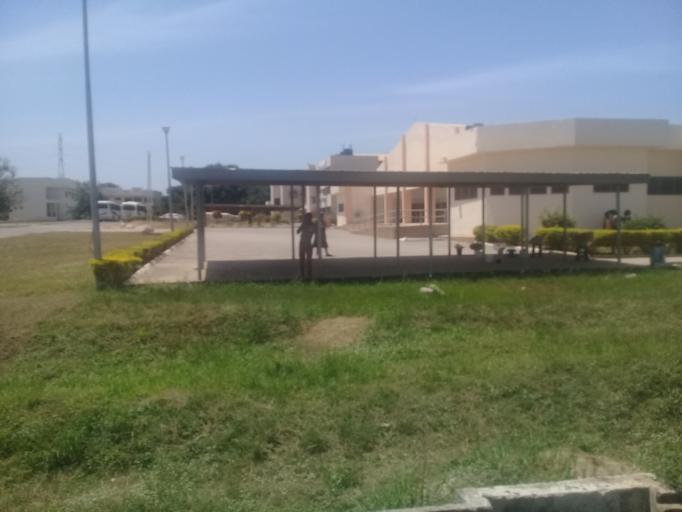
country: GH
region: Central
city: Cape Coast
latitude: 5.1211
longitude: -1.2933
